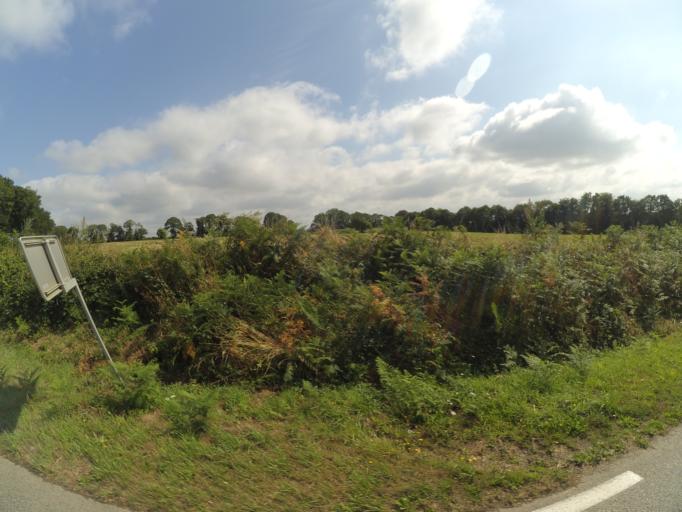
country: FR
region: Brittany
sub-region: Departement du Finistere
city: Mellac
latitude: 47.9084
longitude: -3.5969
